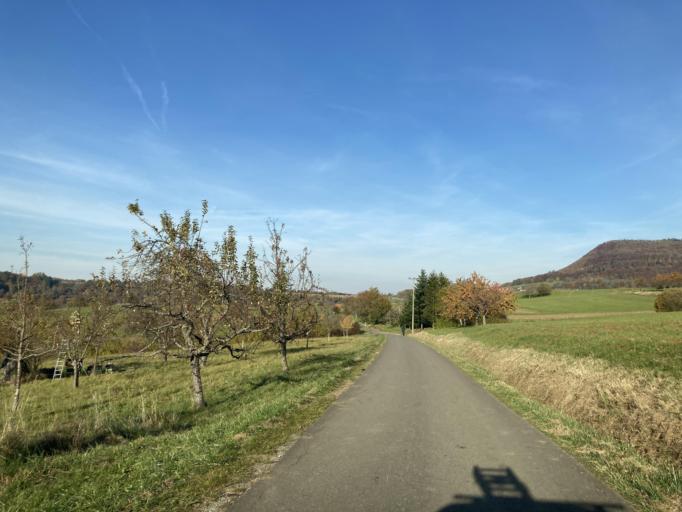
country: DE
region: Baden-Wuerttemberg
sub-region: Tuebingen Region
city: Nehren
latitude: 48.4064
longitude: 9.0991
